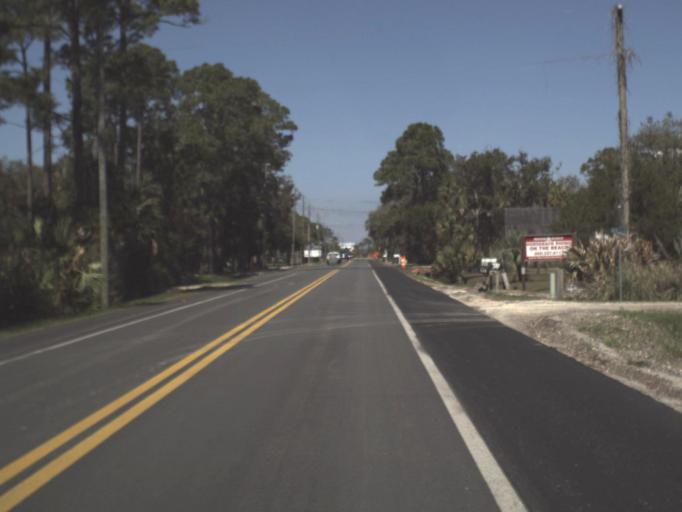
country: US
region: Florida
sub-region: Gulf County
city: Port Saint Joe
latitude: 29.7450
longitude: -85.3020
